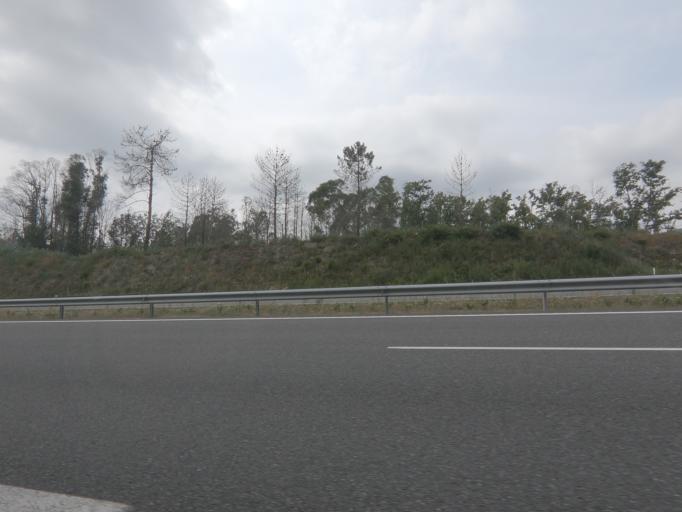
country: ES
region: Galicia
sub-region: Provincia de Pontevedra
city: Covelo
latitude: 42.1681
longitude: -8.3817
